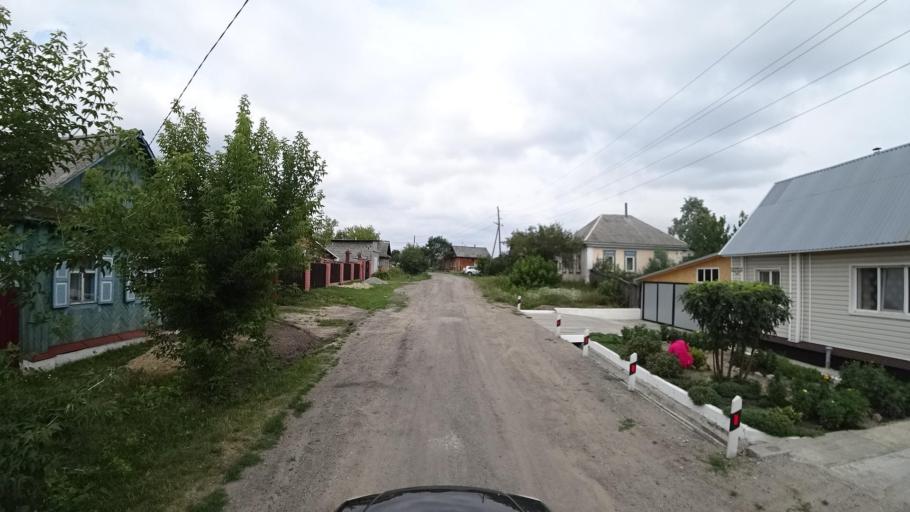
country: RU
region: Sverdlovsk
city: Kamyshlov
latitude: 56.8511
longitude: 62.6790
